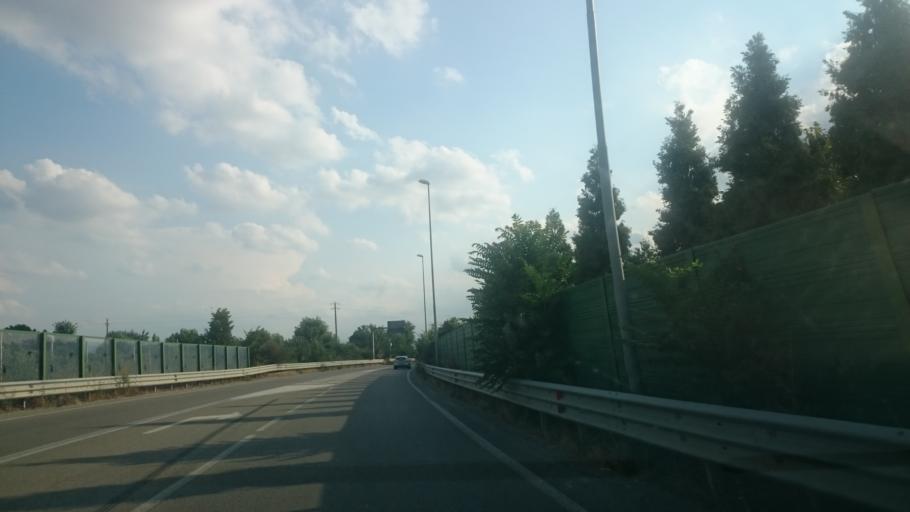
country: IT
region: Emilia-Romagna
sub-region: Provincia di Reggio Emilia
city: Salvaterra
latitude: 44.5991
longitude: 10.7781
